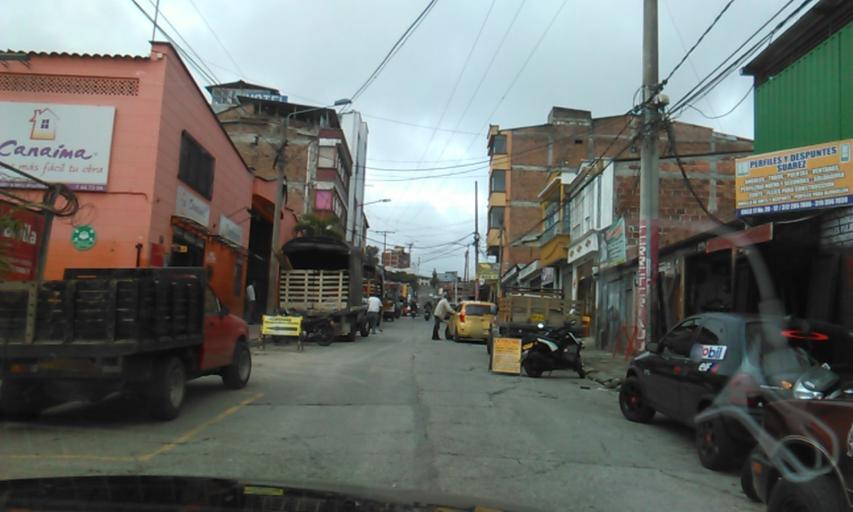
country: CO
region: Quindio
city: Armenia
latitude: 4.5375
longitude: -75.6743
